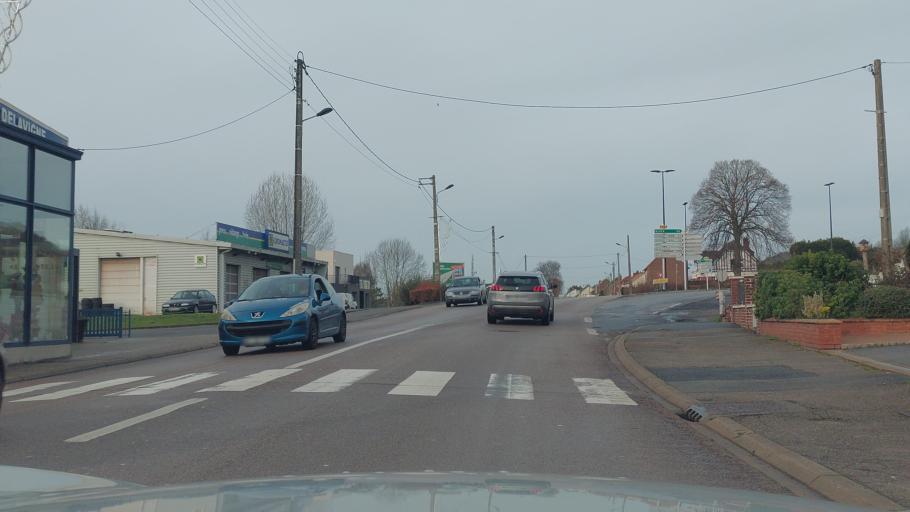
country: FR
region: Haute-Normandie
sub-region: Departement de la Seine-Maritime
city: Eu
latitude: 50.0568
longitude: 1.4224
